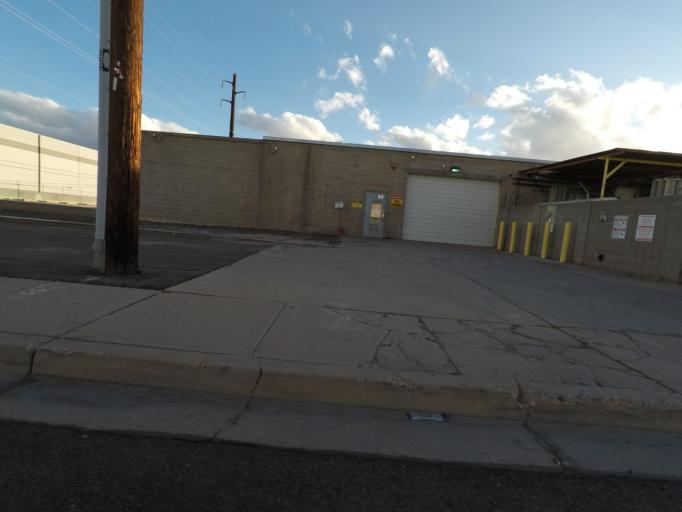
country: US
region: Arizona
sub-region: Maricopa County
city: Glendale
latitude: 33.4993
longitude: -112.1432
